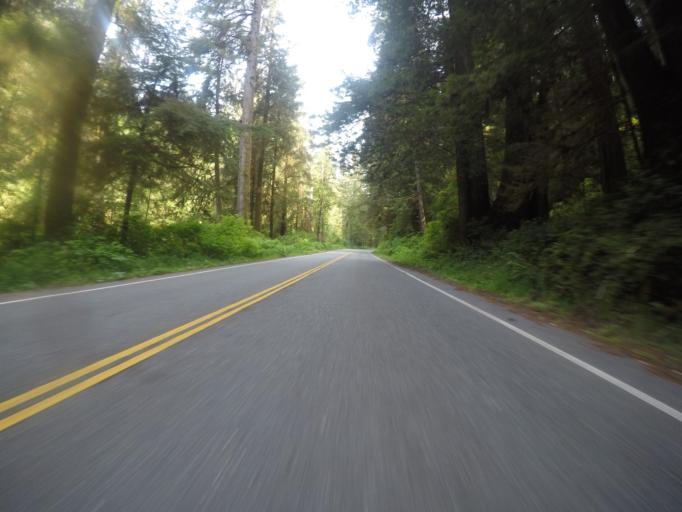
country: US
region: California
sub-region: Del Norte County
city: Bertsch-Oceanview
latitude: 41.4228
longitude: -124.0356
